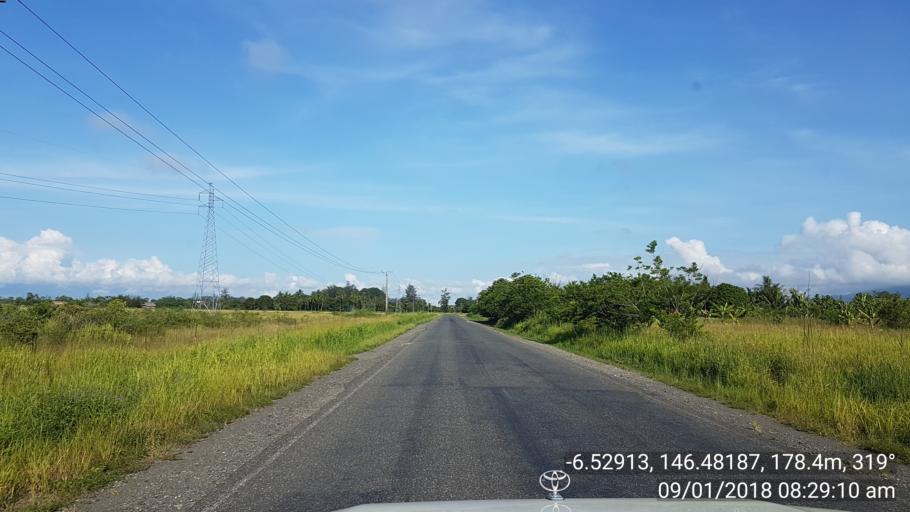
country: PG
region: Morobe
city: Lae
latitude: -6.5289
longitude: 146.4818
